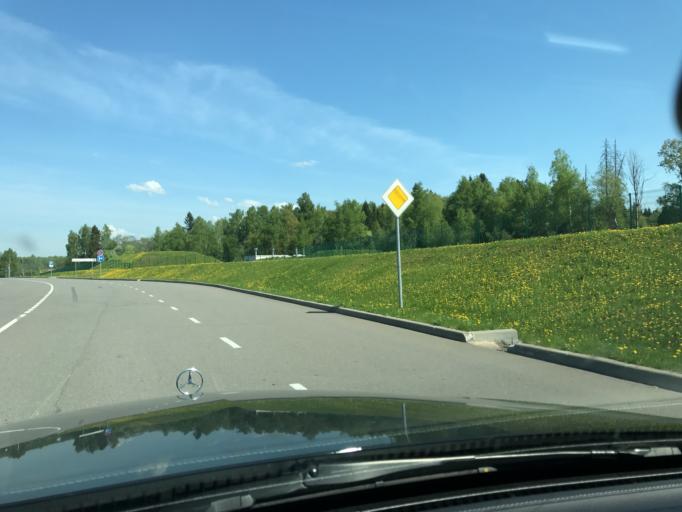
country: RU
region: Moskovskaya
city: Sychevo
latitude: 55.9956
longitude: 36.2722
